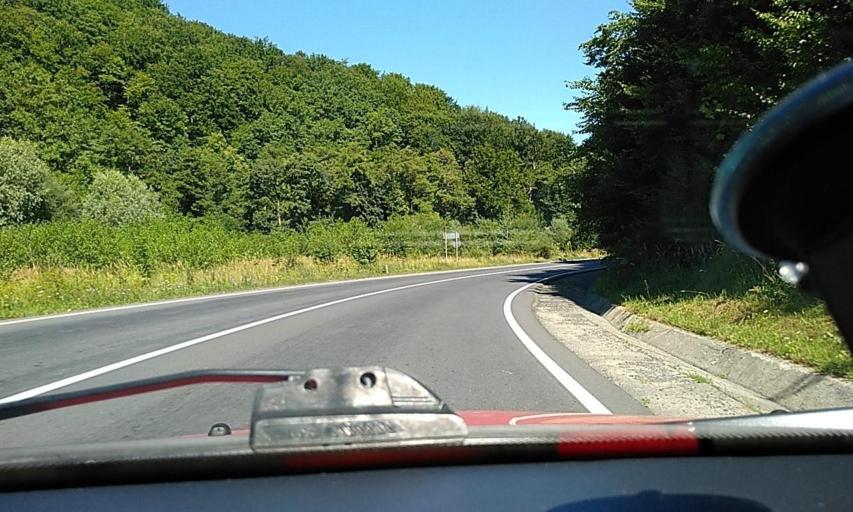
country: RO
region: Brasov
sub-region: Comuna Hoghiz
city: Hoghiz
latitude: 45.9504
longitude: 25.3720
